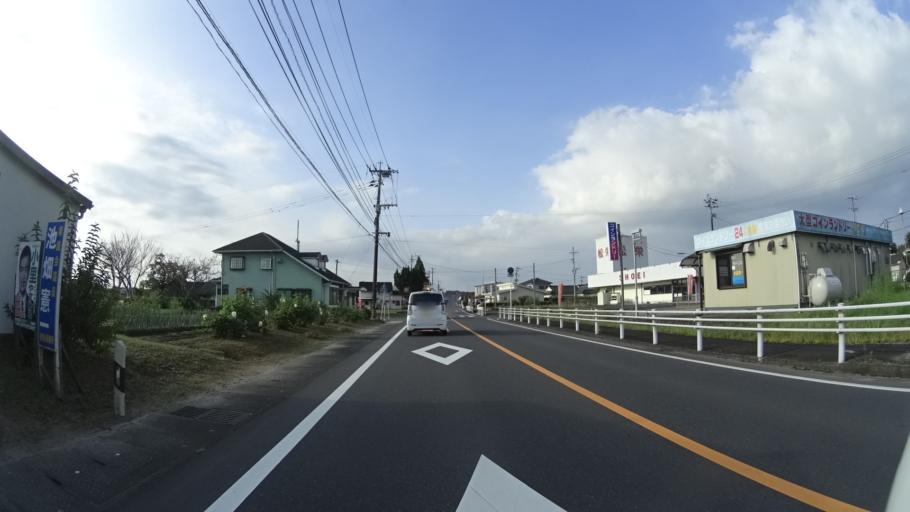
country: JP
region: Kagoshima
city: Okuchi-shinohara
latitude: 32.0343
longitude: 130.5969
